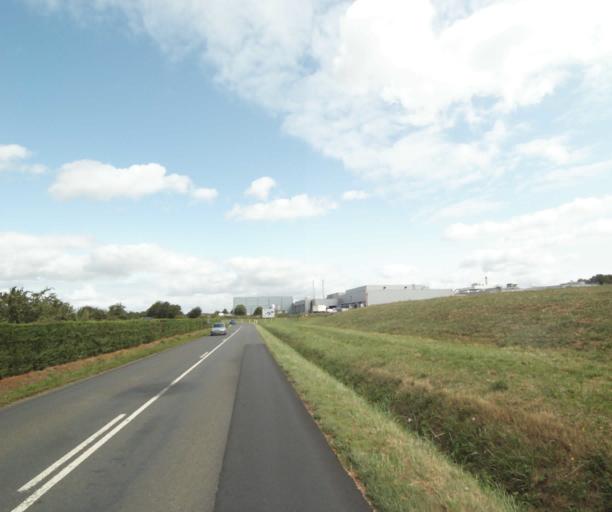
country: FR
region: Pays de la Loire
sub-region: Departement de la Sarthe
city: Sable-sur-Sarthe
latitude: 47.8227
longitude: -0.3182
